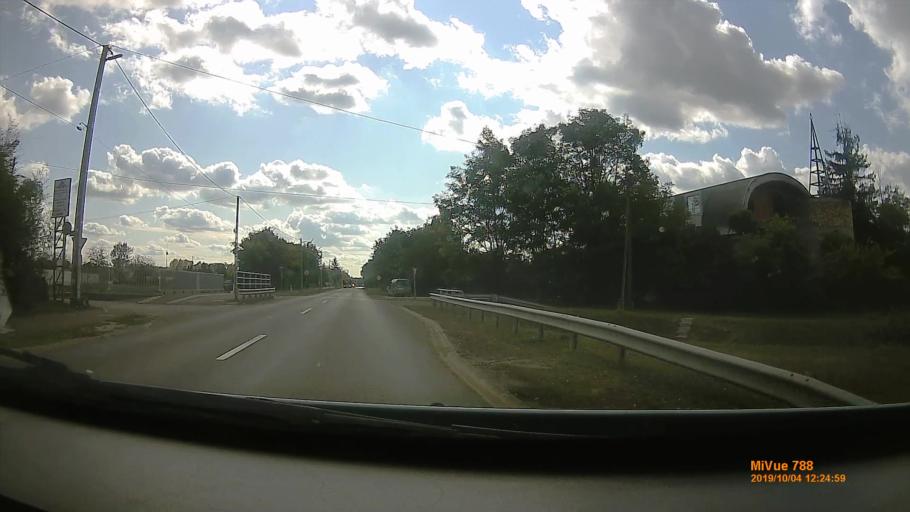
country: HU
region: Szabolcs-Szatmar-Bereg
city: Nyiregyhaza
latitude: 47.9908
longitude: 21.7039
